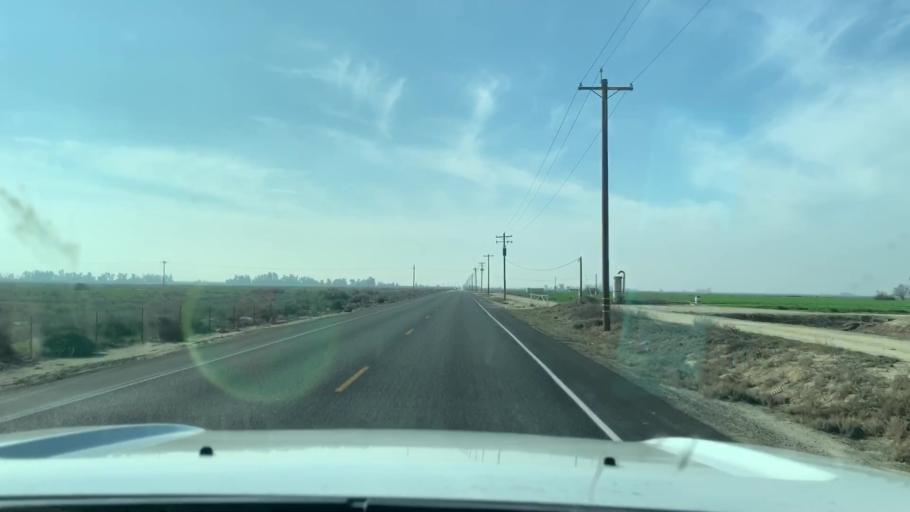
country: US
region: California
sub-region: Kern County
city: Buttonwillow
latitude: 35.4421
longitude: -119.3808
